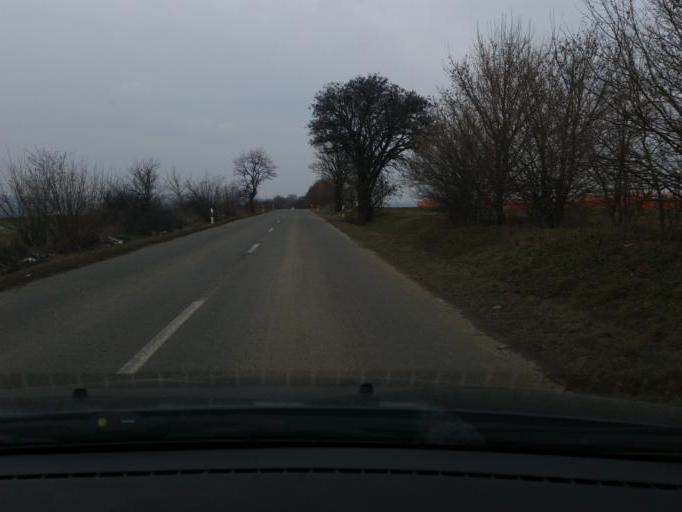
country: HU
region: Pest
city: Perbal
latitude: 47.5676
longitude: 18.7908
